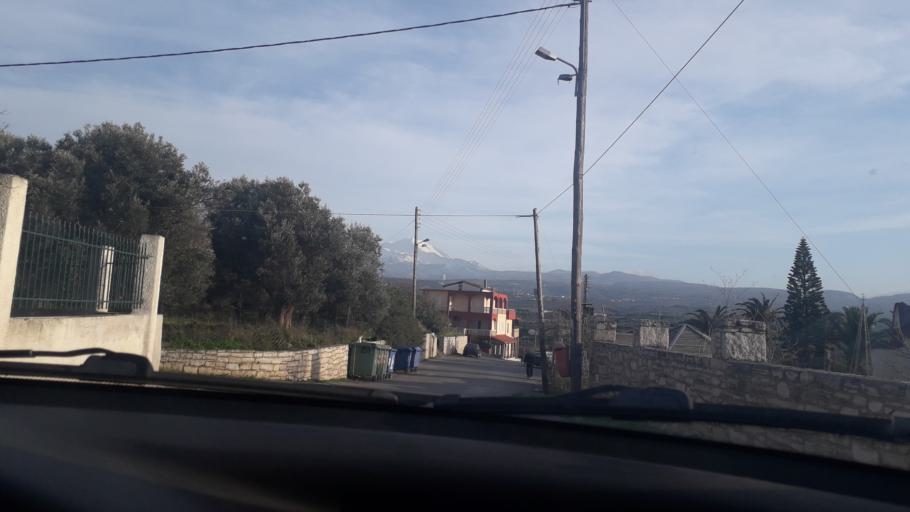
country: GR
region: Crete
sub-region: Nomos Rethymnis
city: Panormos
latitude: 35.3843
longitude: 24.6187
